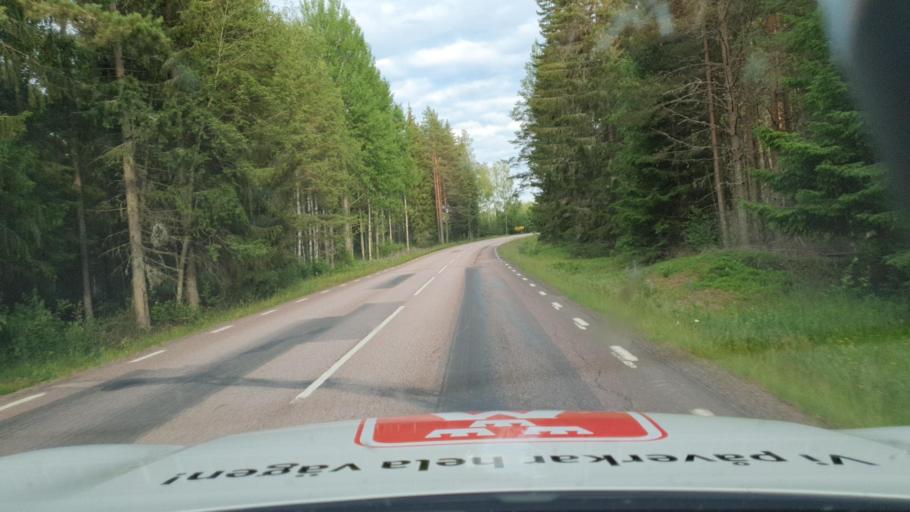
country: SE
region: Vaermland
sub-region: Karlstads Kommun
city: Molkom
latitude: 59.5344
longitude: 13.7868
